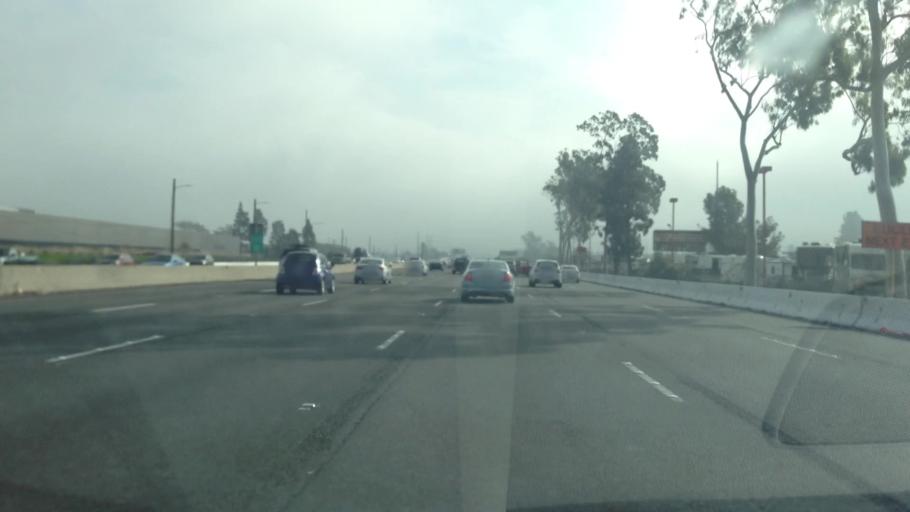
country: US
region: California
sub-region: Orange County
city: Fountain Valley
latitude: 33.6996
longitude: -117.9449
